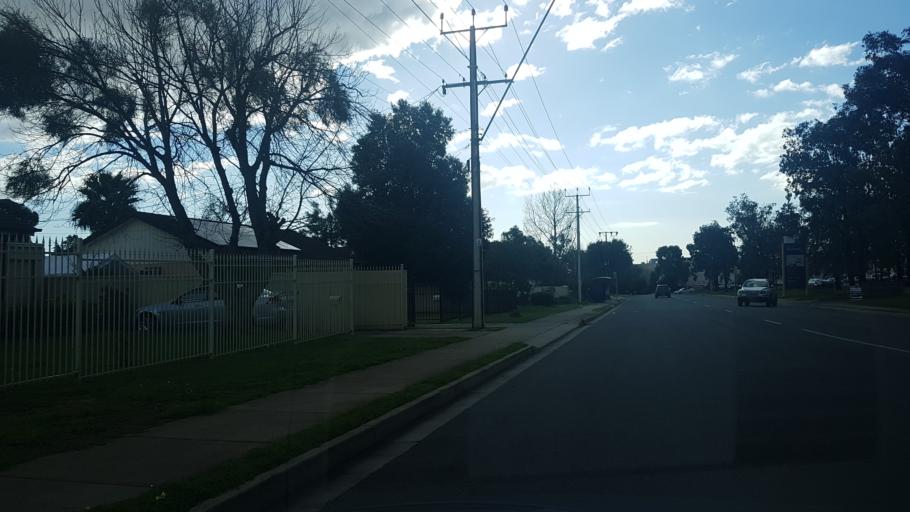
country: AU
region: South Australia
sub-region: Salisbury
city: Ingle Farm
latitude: -34.8328
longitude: 138.6486
